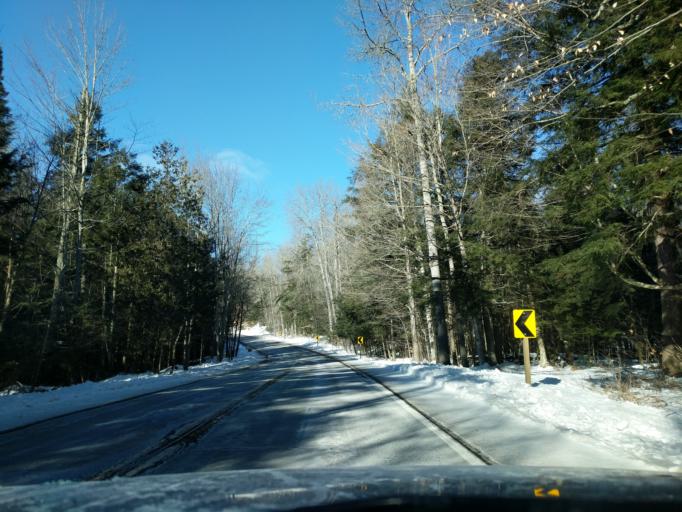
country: US
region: Wisconsin
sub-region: Menominee County
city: Keshena
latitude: 45.1114
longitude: -88.6413
